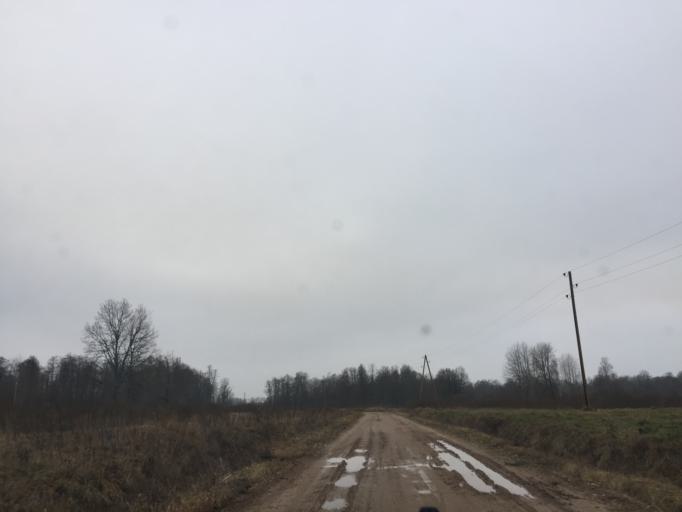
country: LV
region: Limbazu Rajons
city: Limbazi
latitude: 57.5768
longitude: 24.5486
